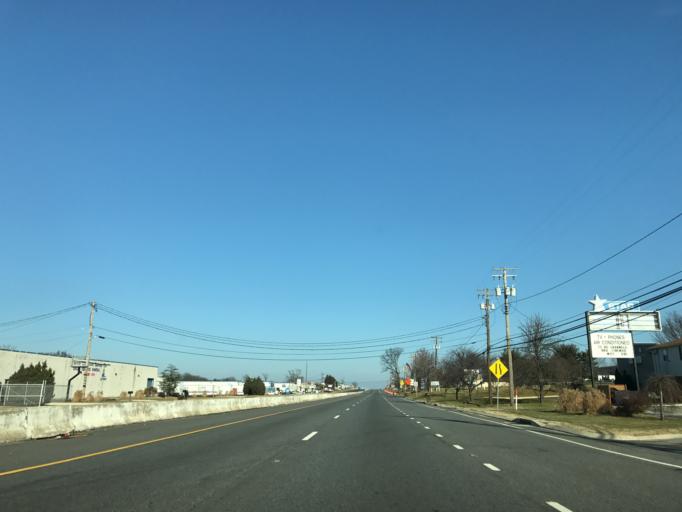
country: US
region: Maryland
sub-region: Baltimore County
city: Middle River
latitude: 39.3540
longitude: -76.4531
